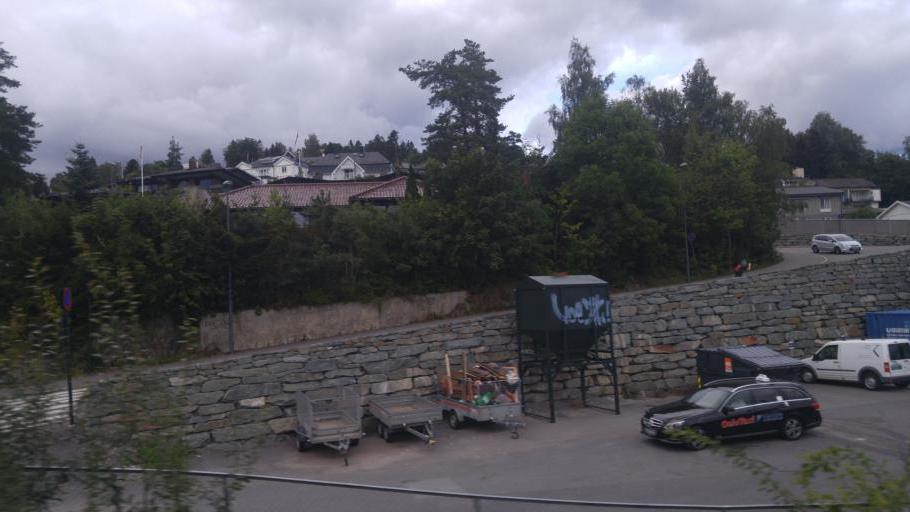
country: NO
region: Oslo
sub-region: Oslo
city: Sjolyststranda
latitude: 59.9575
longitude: 10.6723
